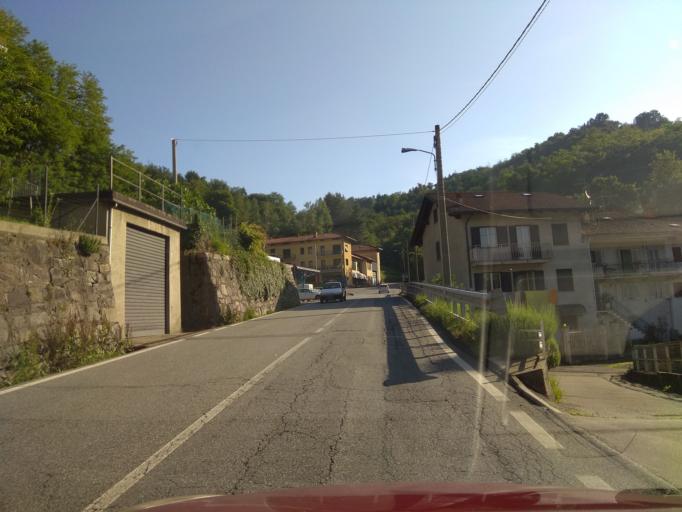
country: IT
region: Piedmont
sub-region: Provincia di Biella
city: Valle Mosso
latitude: 45.6335
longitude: 8.1505
